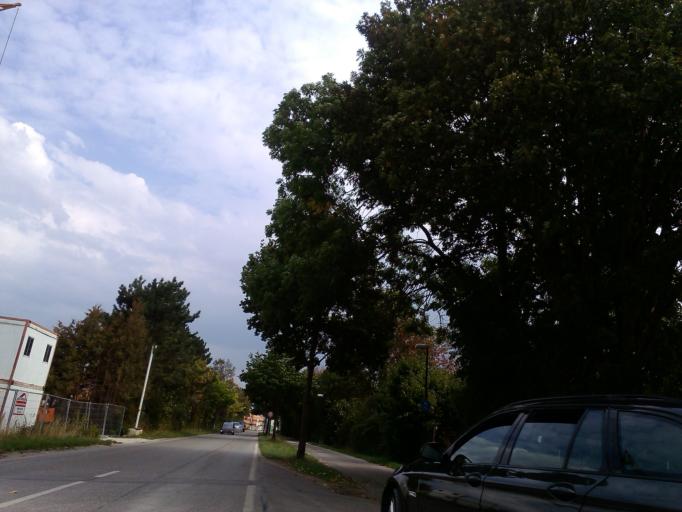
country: DE
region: Bavaria
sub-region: Upper Bavaria
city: Puchheim
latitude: 48.1426
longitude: 11.3550
